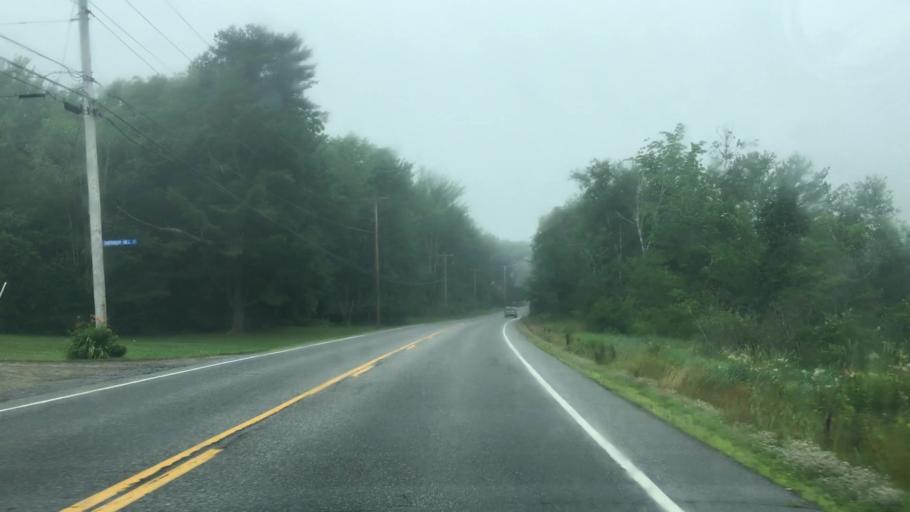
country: US
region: Maine
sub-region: Lincoln County
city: Boothbay
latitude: 43.8877
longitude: -69.6296
